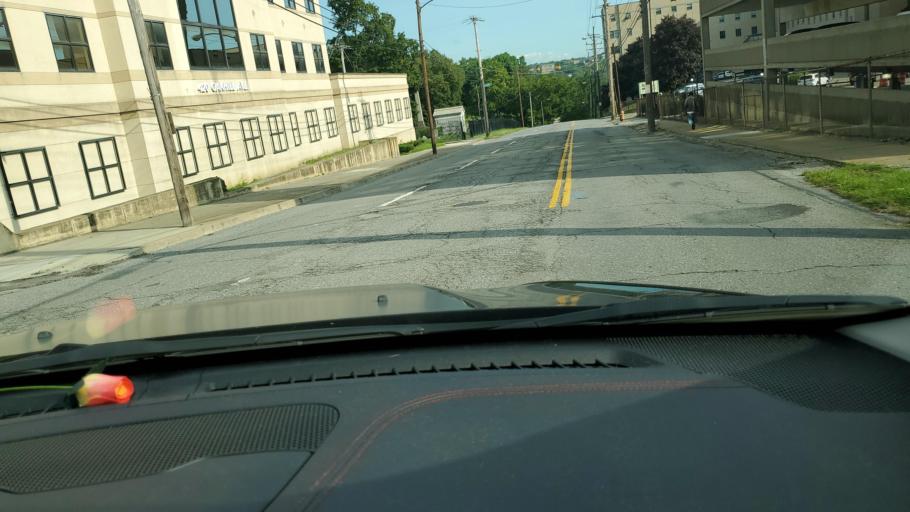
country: US
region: Ohio
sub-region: Mahoning County
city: Youngstown
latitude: 41.0952
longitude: -80.6595
